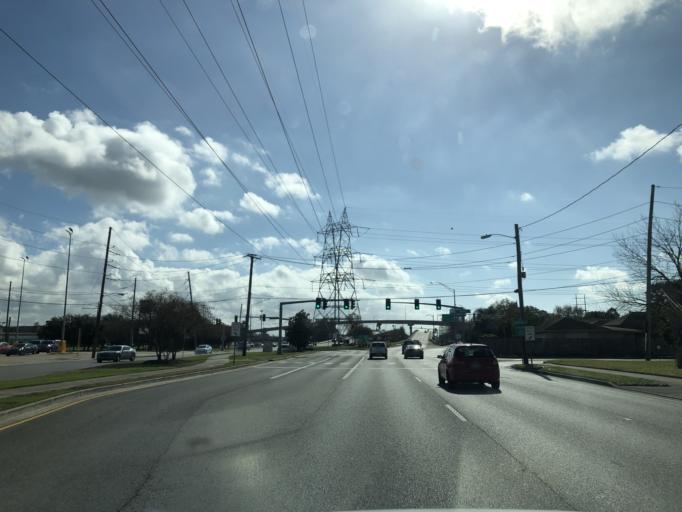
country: US
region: Louisiana
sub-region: Jefferson Parish
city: Kenner
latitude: 30.0118
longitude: -90.2225
